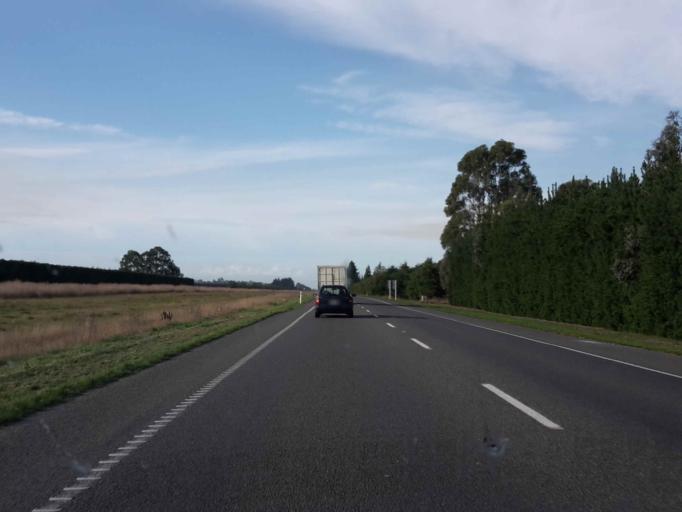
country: NZ
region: Canterbury
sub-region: Ashburton District
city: Tinwald
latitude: -43.9441
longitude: 171.6759
